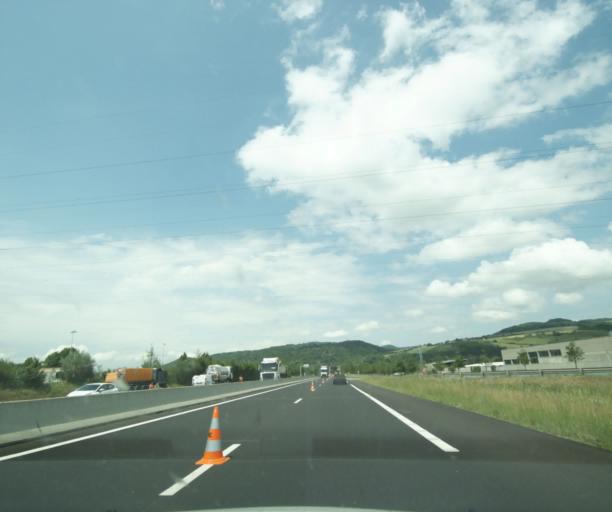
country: FR
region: Auvergne
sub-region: Departement du Puy-de-Dome
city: Issoire
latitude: 45.5539
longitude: 3.2685
